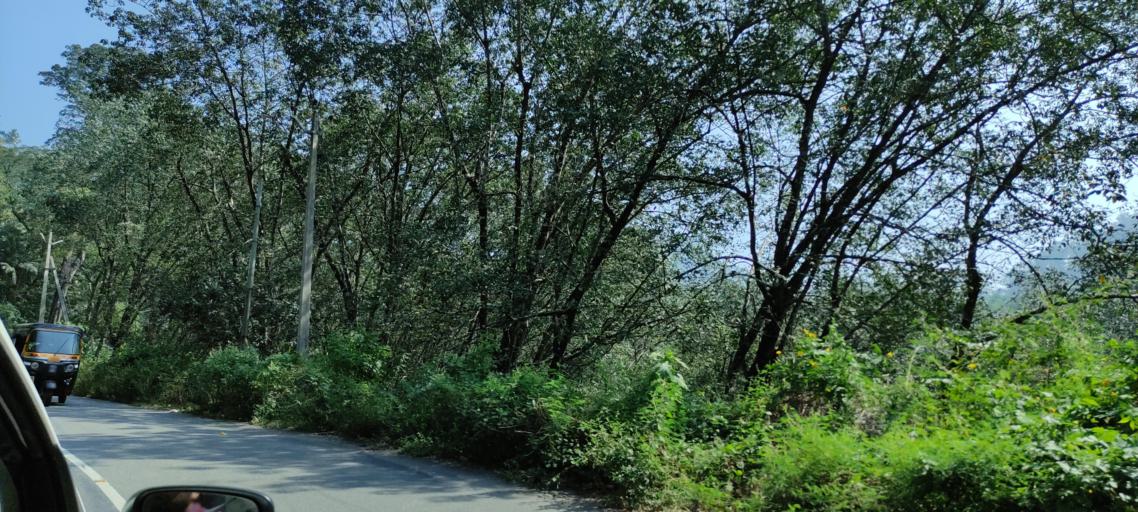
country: IN
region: Kerala
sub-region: Kollam
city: Punalur
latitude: 8.9717
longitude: 77.0662
